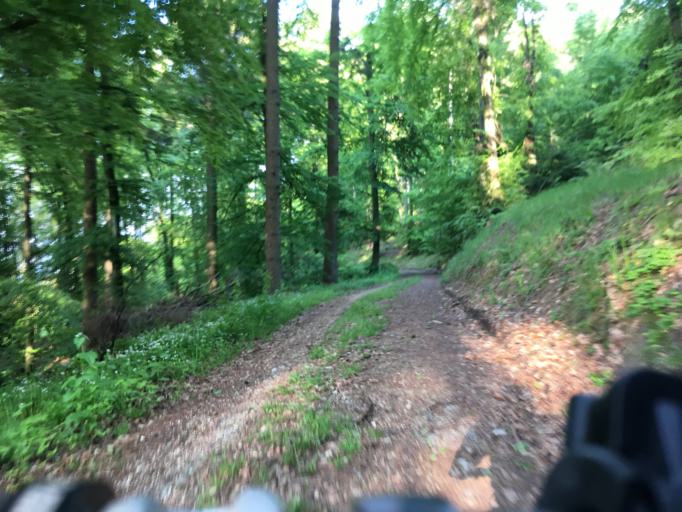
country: CH
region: Schaffhausen
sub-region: Bezirk Stein
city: Ramsen
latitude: 47.7045
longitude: 8.7873
